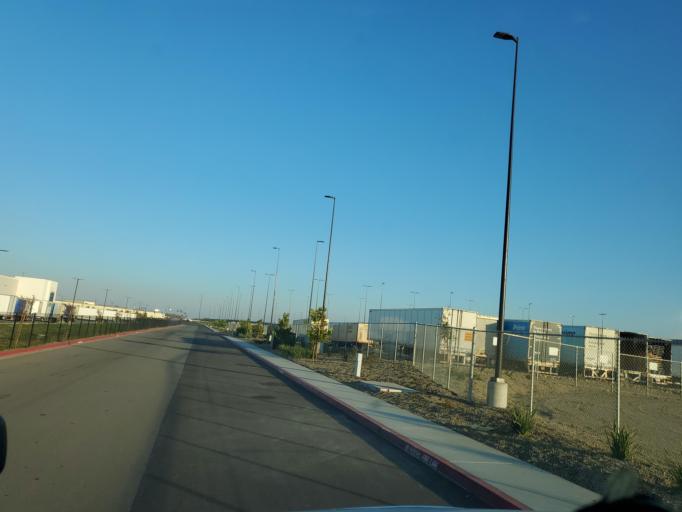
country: US
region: California
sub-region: San Joaquin County
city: Kennedy
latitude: 37.9126
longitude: -121.1919
